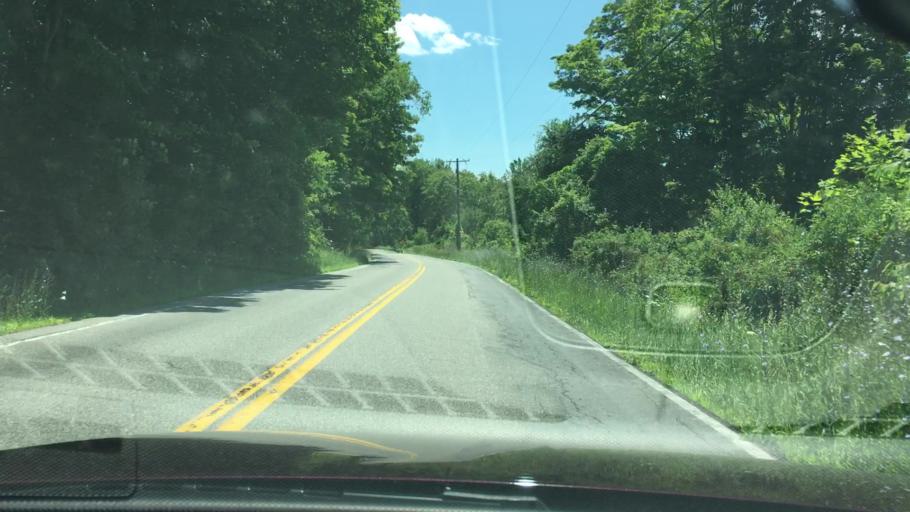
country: US
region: New York
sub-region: Putnam County
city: Lake Carmel
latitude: 41.4927
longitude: -73.6625
